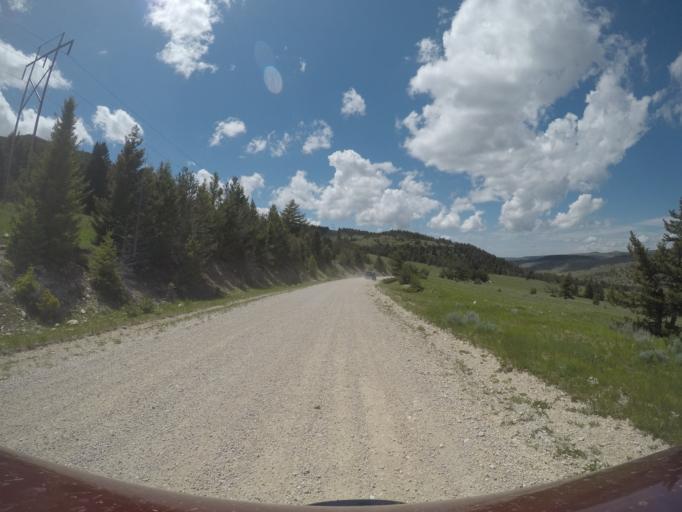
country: US
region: Wyoming
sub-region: Big Horn County
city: Lovell
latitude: 45.2050
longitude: -108.5364
